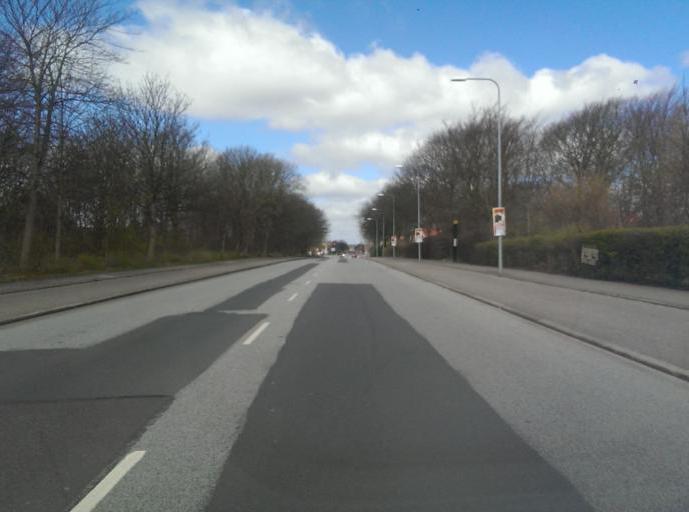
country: DK
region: South Denmark
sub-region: Esbjerg Kommune
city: Esbjerg
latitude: 55.4767
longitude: 8.4325
